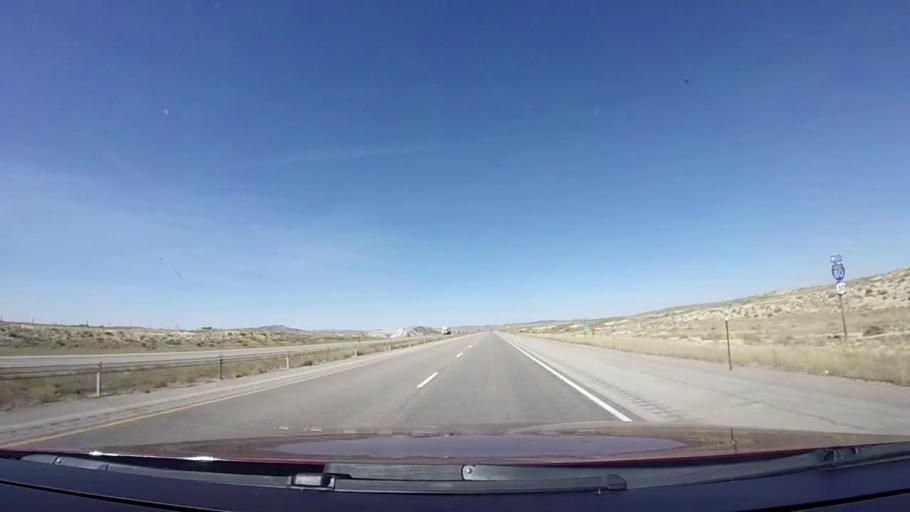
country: US
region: Wyoming
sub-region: Sweetwater County
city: Rock Springs
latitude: 41.6476
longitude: -108.6414
